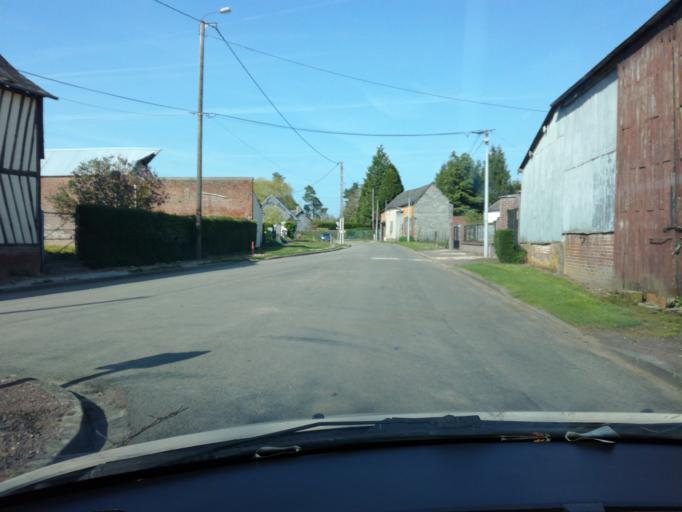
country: FR
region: Picardie
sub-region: Departement de la Somme
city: Hornoy-le-Bourg
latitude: 49.8277
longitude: 1.9382
